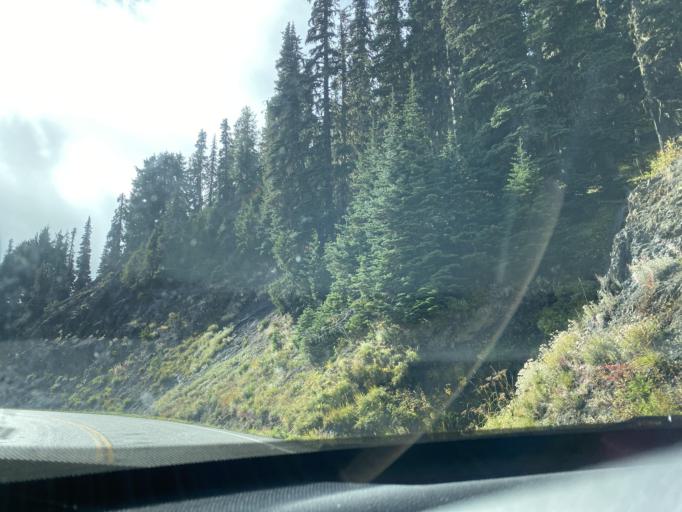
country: US
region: Washington
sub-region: Clallam County
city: Port Angeles
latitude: 47.9767
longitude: -123.4769
